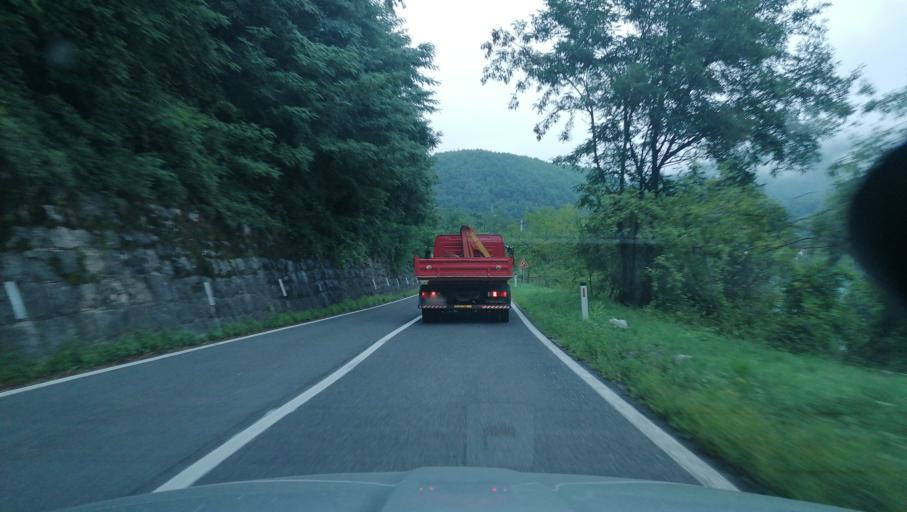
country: BA
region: Federation of Bosnia and Herzegovina
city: Jablanica
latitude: 43.7210
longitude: 17.7067
